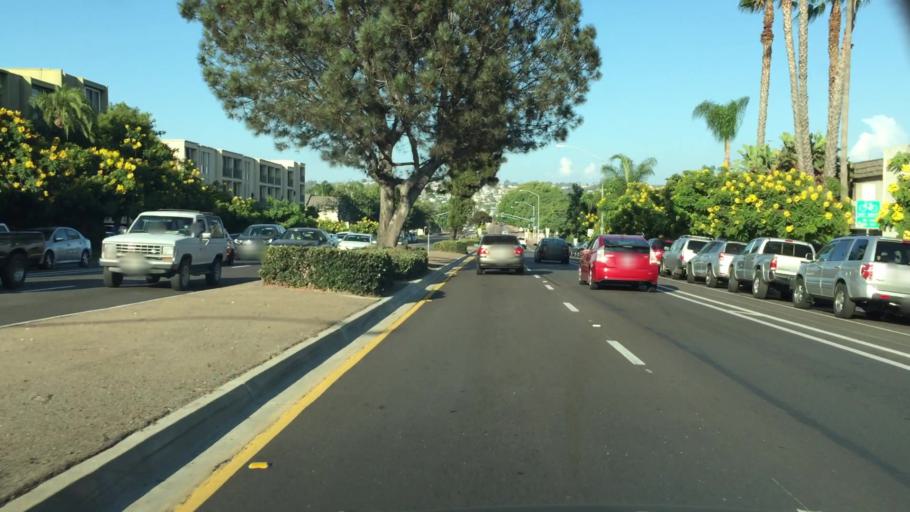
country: US
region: California
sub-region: San Diego County
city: La Jolla
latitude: 32.8005
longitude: -117.2282
